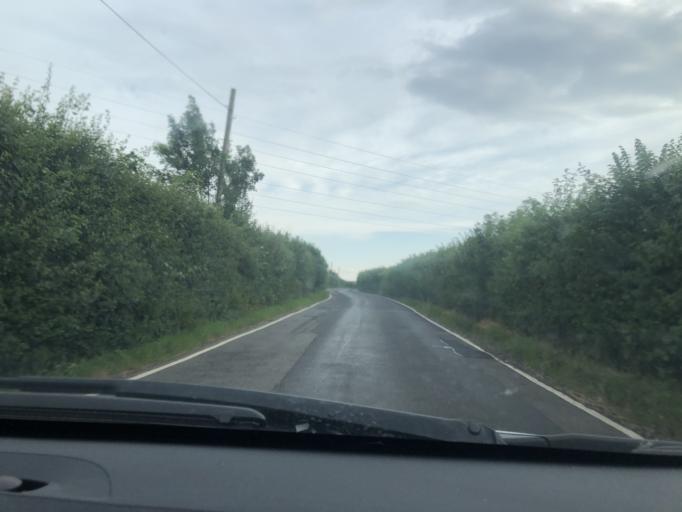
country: GB
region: England
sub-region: Kent
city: Sturry
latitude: 51.3171
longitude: 1.1413
